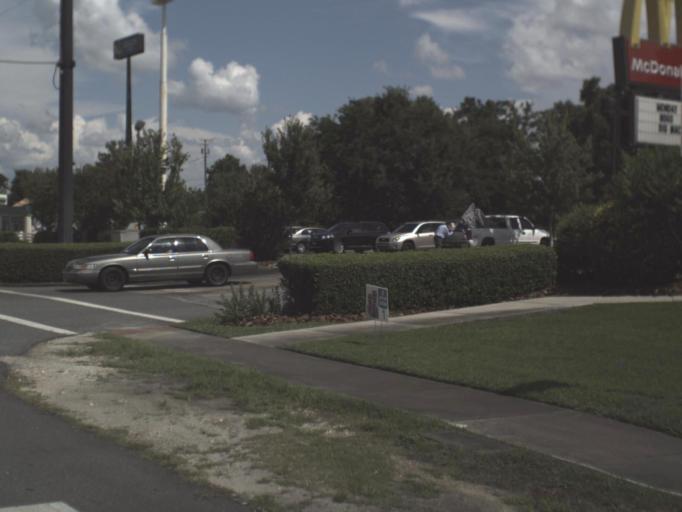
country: US
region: Florida
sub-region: Alachua County
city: High Springs
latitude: 29.8013
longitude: -82.5127
